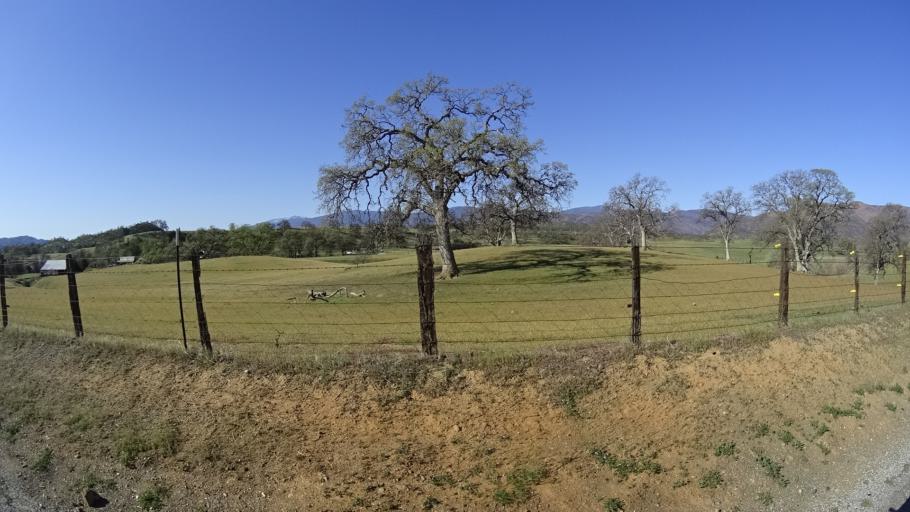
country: US
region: California
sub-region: Glenn County
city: Orland
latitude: 39.6863
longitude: -122.5408
